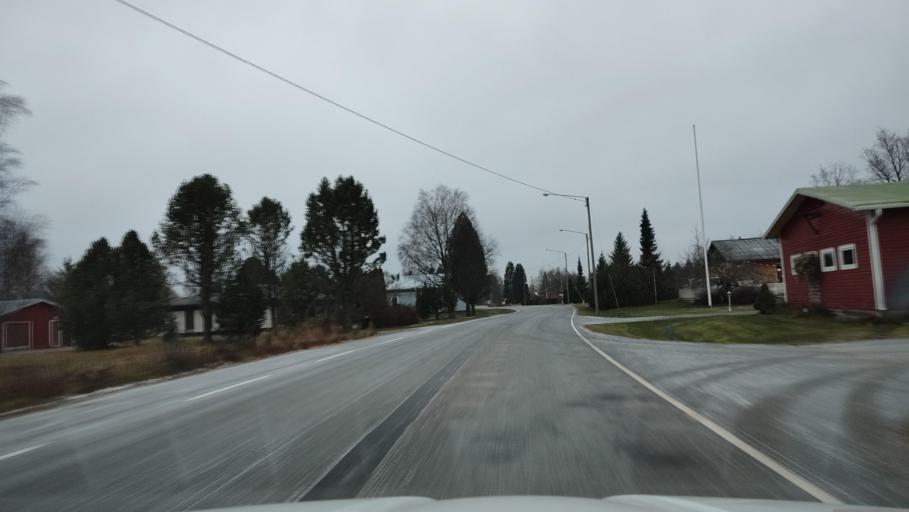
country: FI
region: Southern Ostrobothnia
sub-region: Suupohja
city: Karijoki
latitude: 62.2342
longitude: 21.6504
